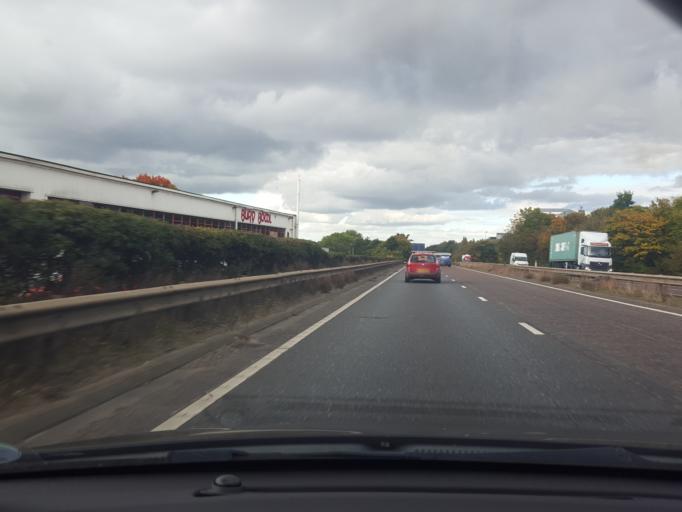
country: GB
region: England
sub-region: Suffolk
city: Bury St Edmunds
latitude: 52.2463
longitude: 0.7249
